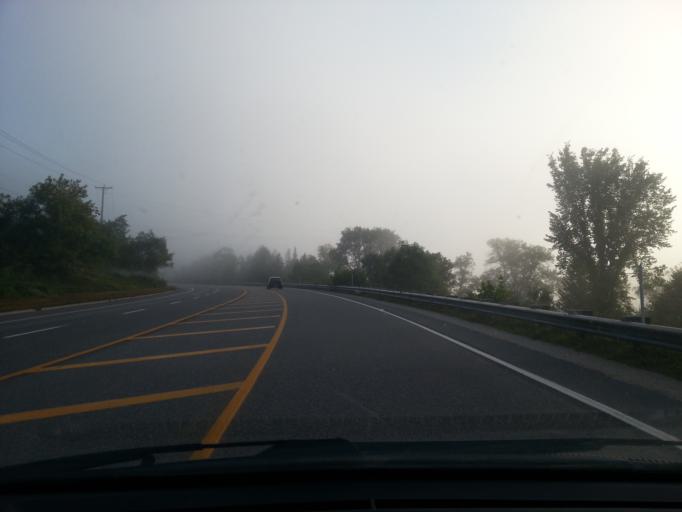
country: CA
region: Quebec
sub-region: Outaouais
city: Wakefield
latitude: 45.7073
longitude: -75.9216
